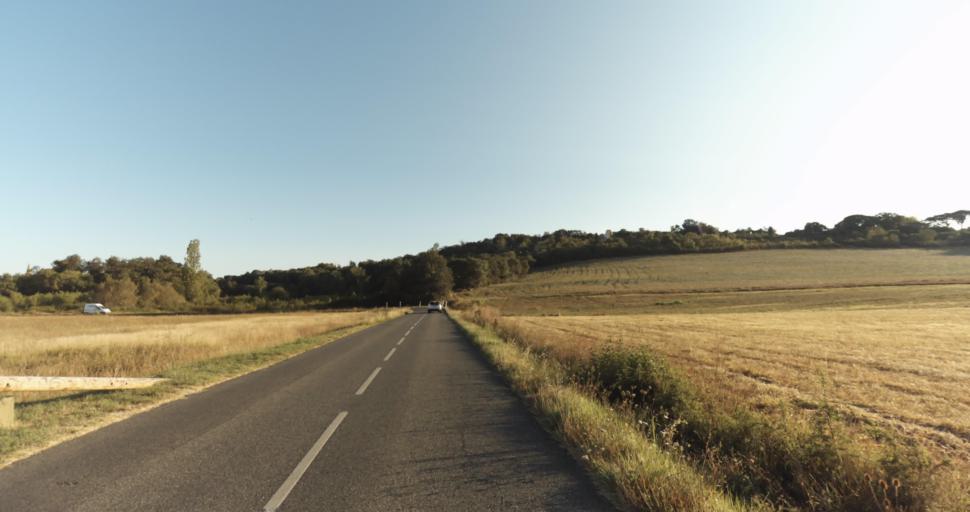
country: FR
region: Midi-Pyrenees
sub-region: Departement de la Haute-Garonne
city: Launaguet
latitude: 43.6689
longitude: 1.4641
